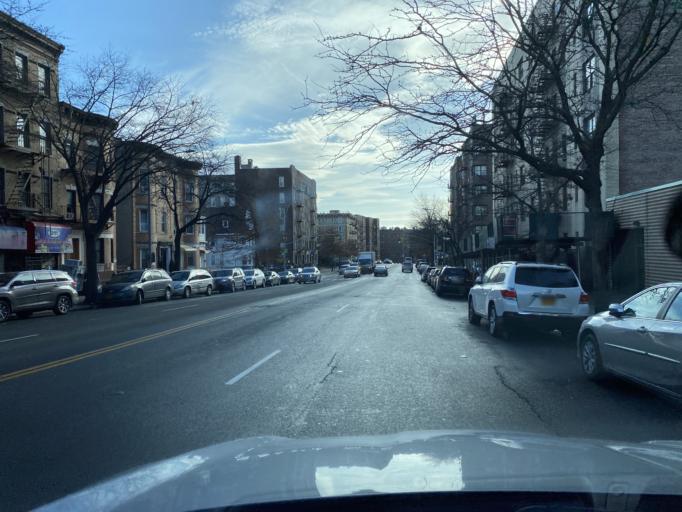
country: US
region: New York
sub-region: Bronx
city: The Bronx
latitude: 40.8713
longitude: -73.8869
